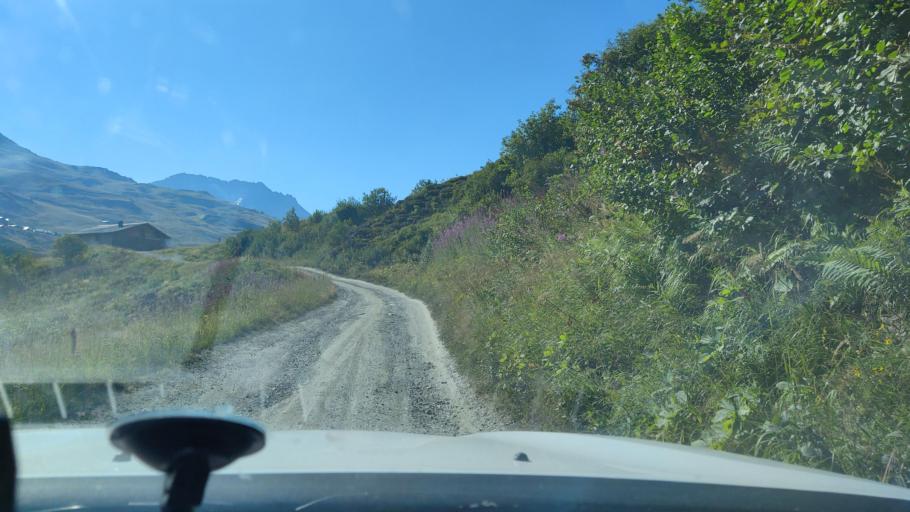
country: FR
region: Rhone-Alpes
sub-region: Departement de la Savoie
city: Val Thorens
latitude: 45.3212
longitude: 6.5287
